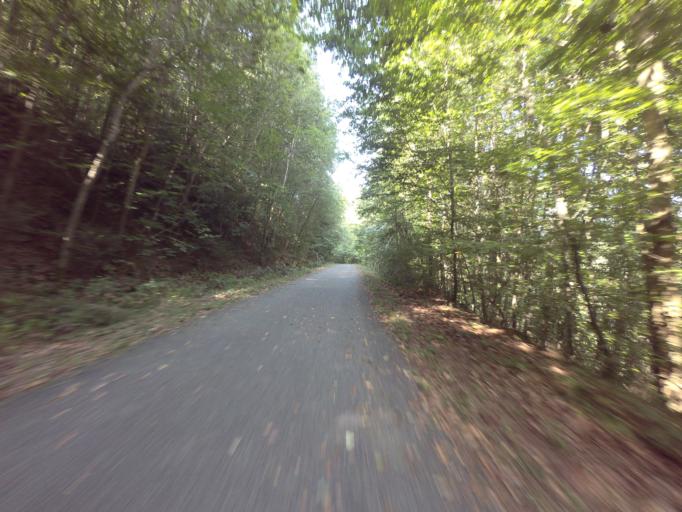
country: CZ
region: Jihocesky
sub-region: Okres Ceske Budejovice
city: Hluboka nad Vltavou
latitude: 49.0929
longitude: 14.4621
